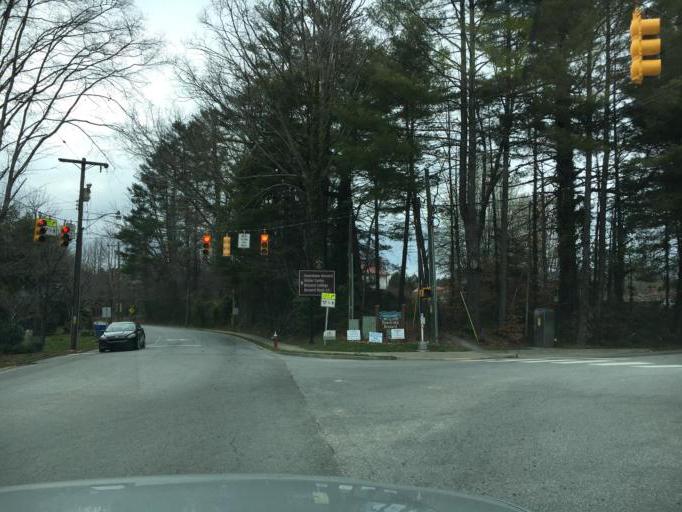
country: US
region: North Carolina
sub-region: Transylvania County
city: Brevard
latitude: 35.2273
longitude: -82.7255
